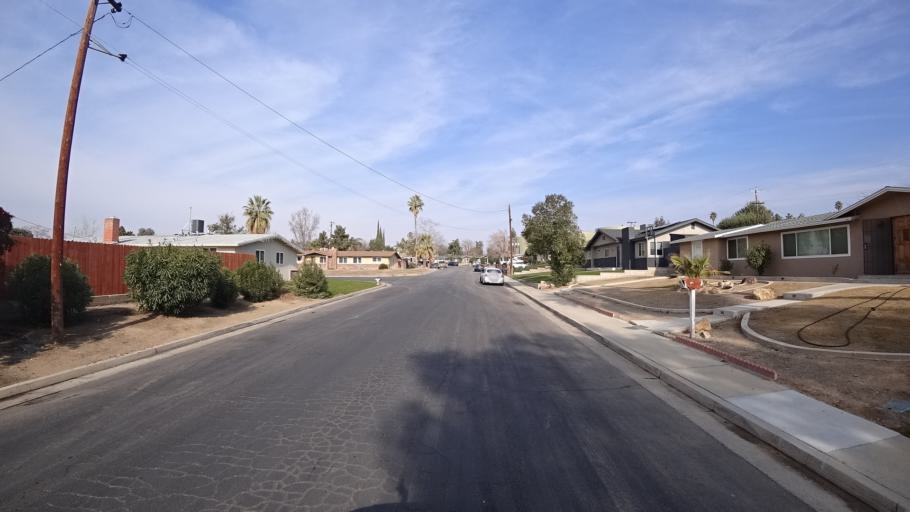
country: US
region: California
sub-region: Kern County
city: Oildale
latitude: 35.4031
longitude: -118.9597
